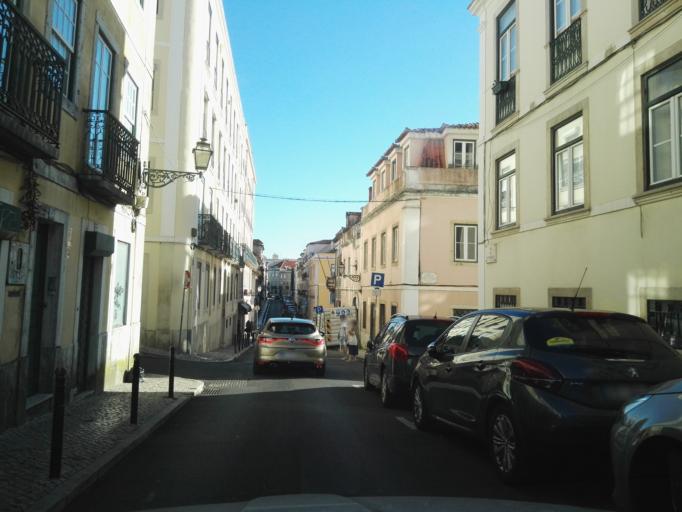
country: PT
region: Lisbon
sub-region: Lisbon
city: Lisbon
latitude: 38.7157
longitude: -9.1507
